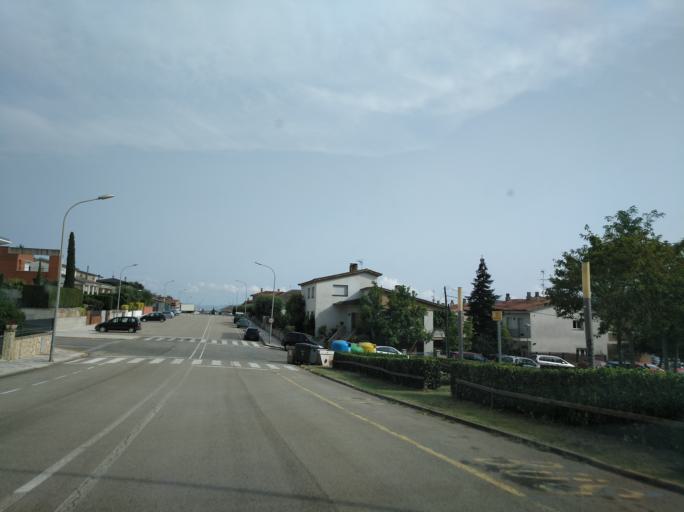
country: ES
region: Catalonia
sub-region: Provincia de Girona
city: Santa Coloma de Farners
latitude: 41.8637
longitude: 2.6675
